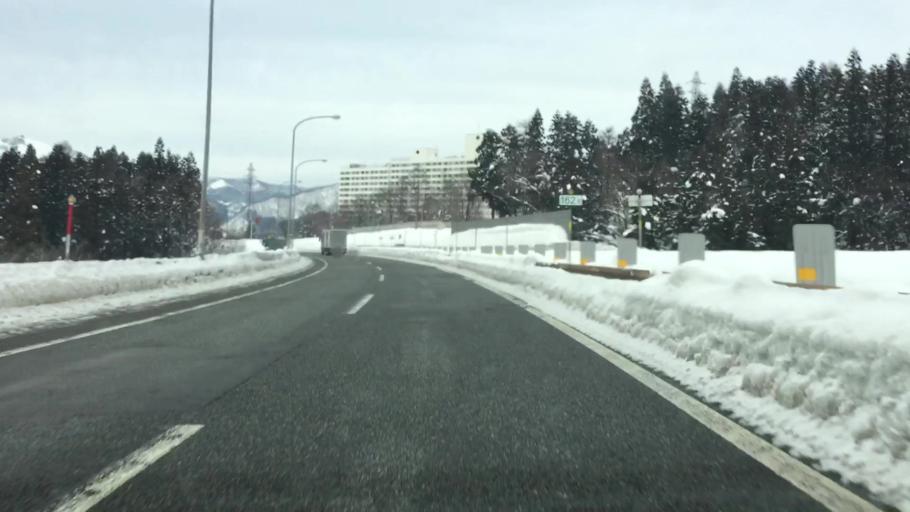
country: JP
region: Niigata
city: Shiozawa
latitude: 36.9009
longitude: 138.8474
